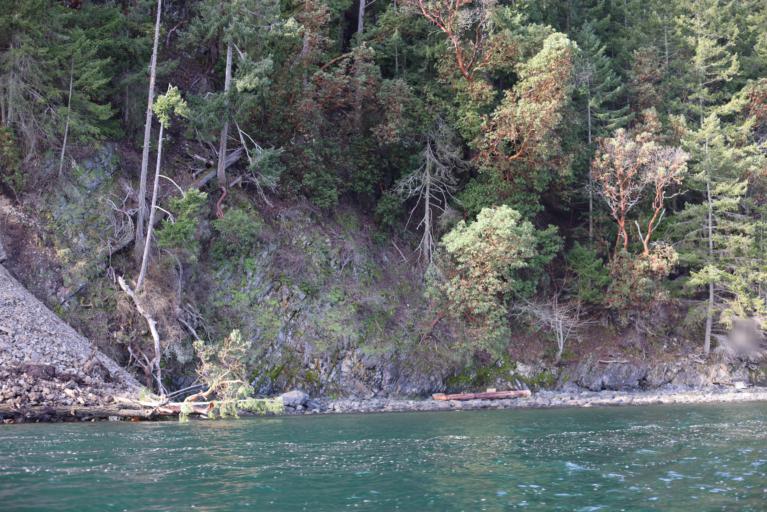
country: CA
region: British Columbia
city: Duncan
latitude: 48.7488
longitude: -123.5691
